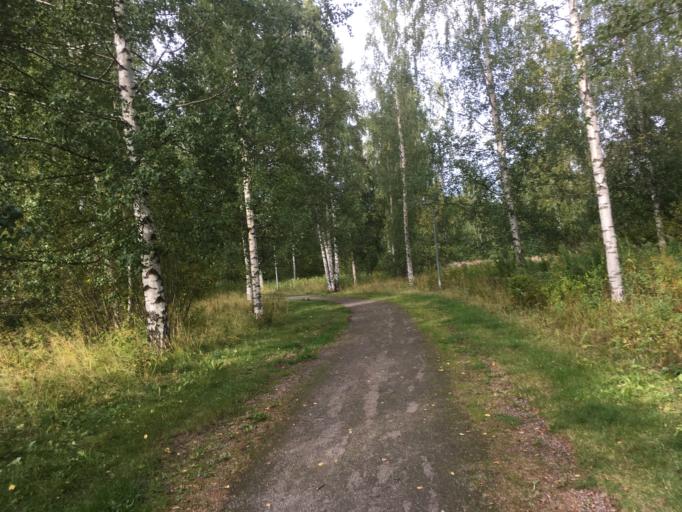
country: FI
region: Central Finland
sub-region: Jyvaeskylae
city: Jyvaeskylae
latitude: 62.2247
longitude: 25.7924
